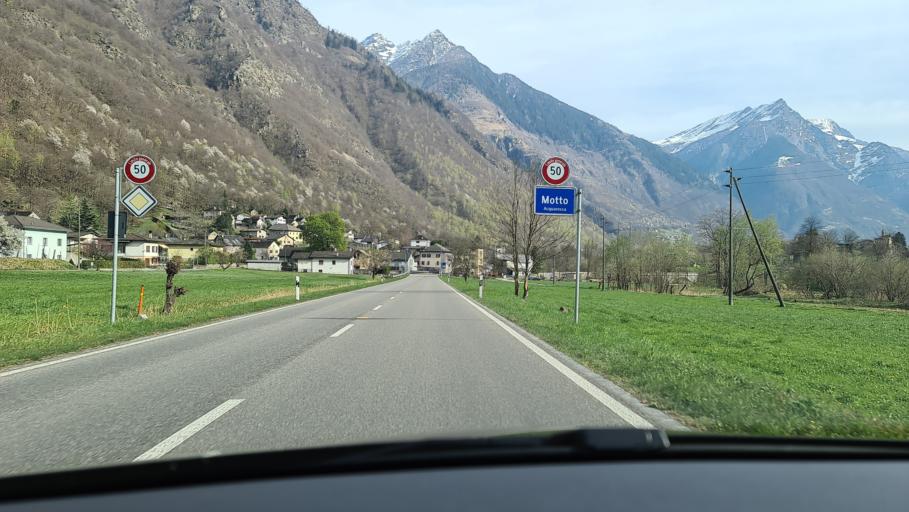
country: CH
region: Ticino
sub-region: Blenio District
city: Malvaglia
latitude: 46.4299
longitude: 8.9681
